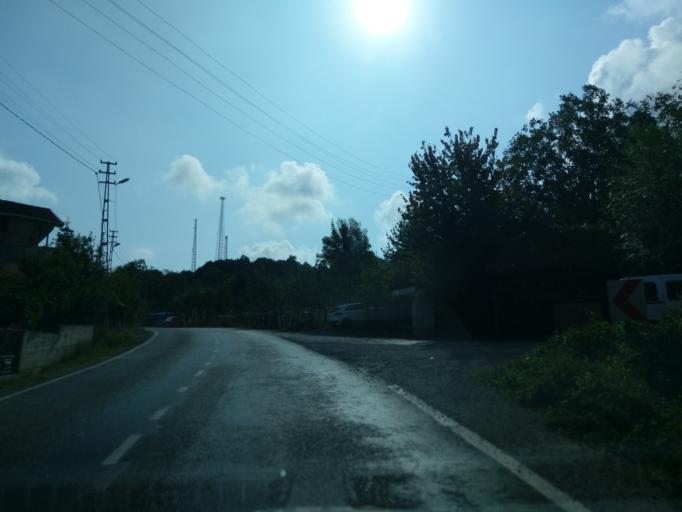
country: TR
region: Sinop
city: Ayancik
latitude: 41.8784
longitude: 34.5092
